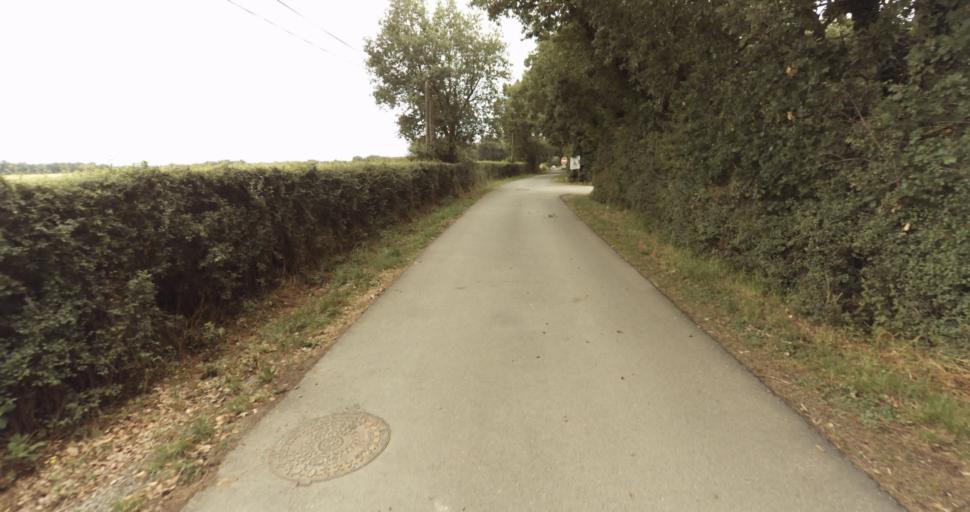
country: FR
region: Midi-Pyrenees
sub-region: Departement de la Haute-Garonne
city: Fonsorbes
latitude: 43.5562
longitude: 1.2416
